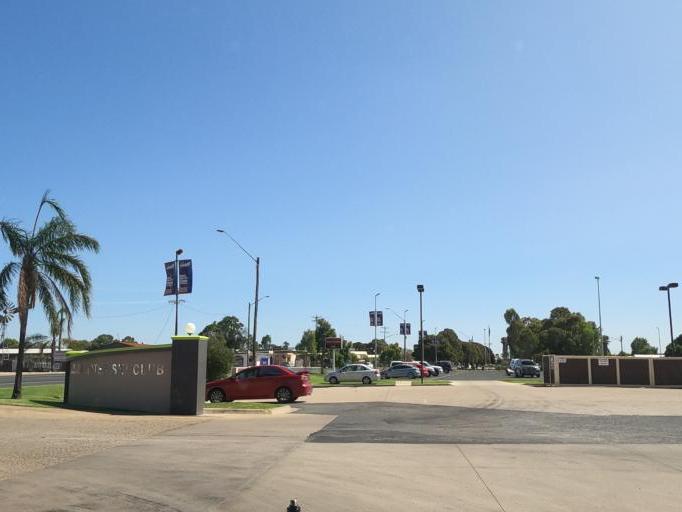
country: AU
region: New South Wales
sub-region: Corowa Shire
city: Mulwala
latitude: -35.9951
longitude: 146.0014
